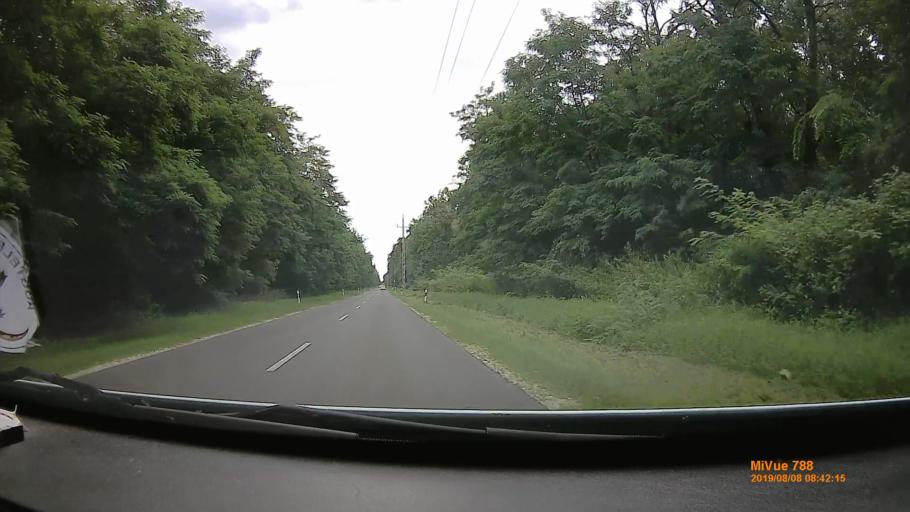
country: HU
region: Hajdu-Bihar
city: Debrecen
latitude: 47.5712
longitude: 21.6307
